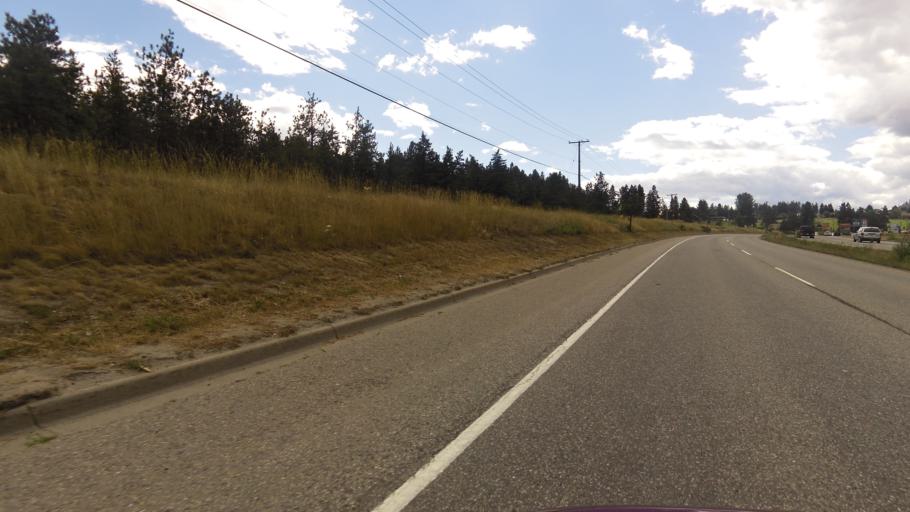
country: CA
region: British Columbia
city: West Kelowna
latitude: 49.8765
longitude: -119.5396
